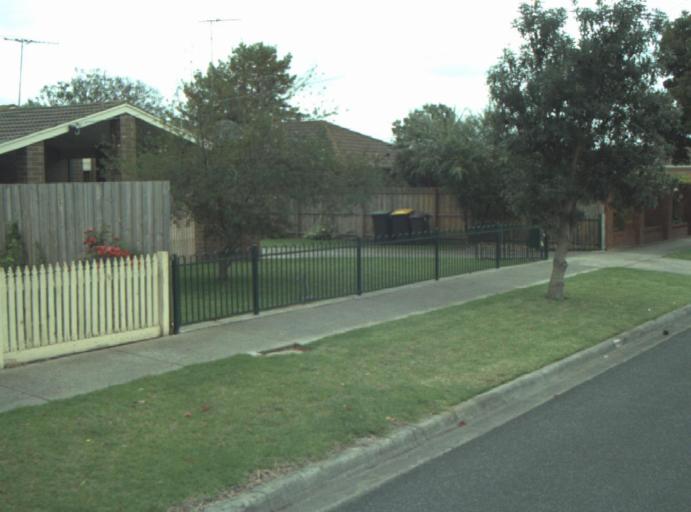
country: AU
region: Victoria
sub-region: Greater Geelong
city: Bell Post Hill
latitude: -38.0675
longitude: 144.3494
